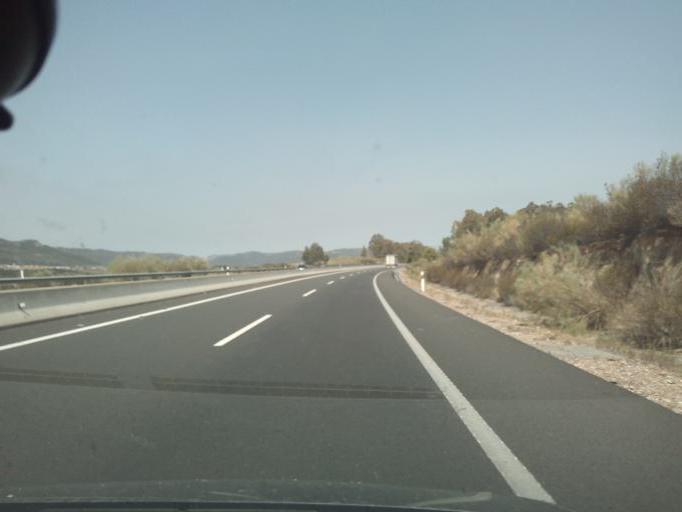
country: ES
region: Extremadura
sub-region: Provincia de Caceres
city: Romangordo
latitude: 39.7175
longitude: -5.7082
